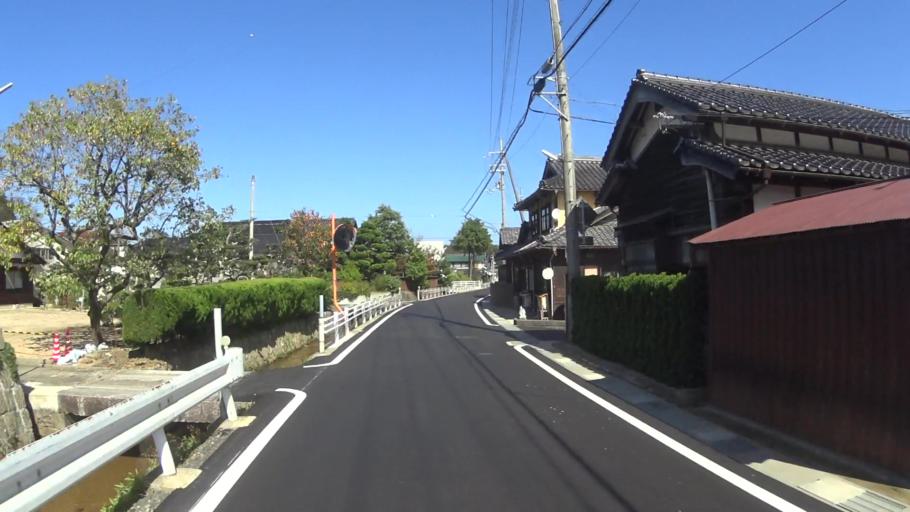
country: JP
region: Kyoto
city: Miyazu
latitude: 35.6805
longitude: 135.0521
